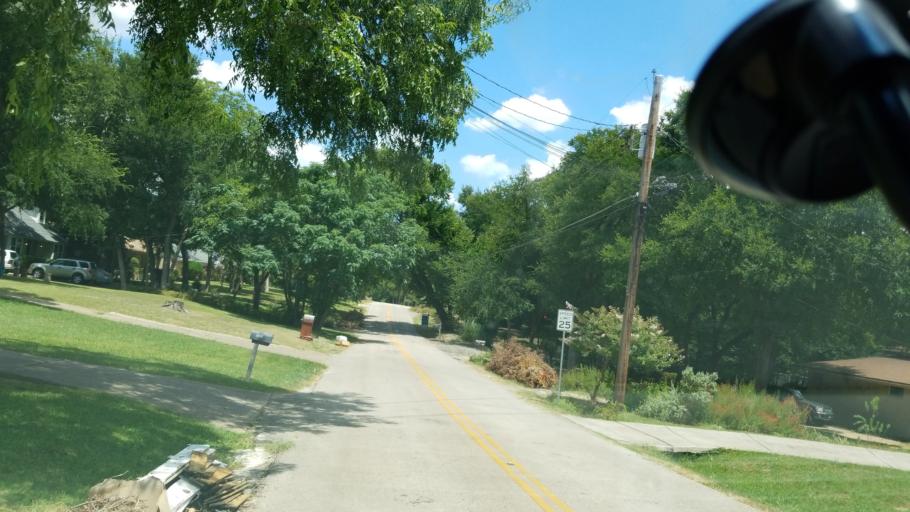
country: US
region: Texas
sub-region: Dallas County
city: Cockrell Hill
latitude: 32.6945
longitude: -96.8690
